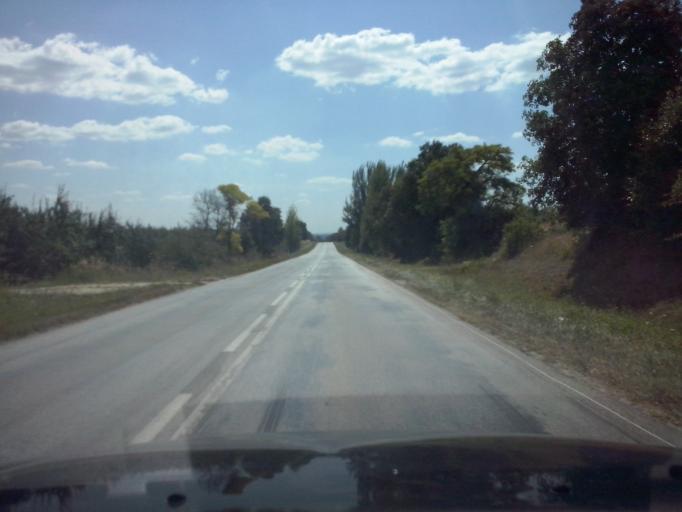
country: PL
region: Swietokrzyskie
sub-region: Powiat staszowski
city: Szydlow
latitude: 50.6057
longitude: 21.0097
